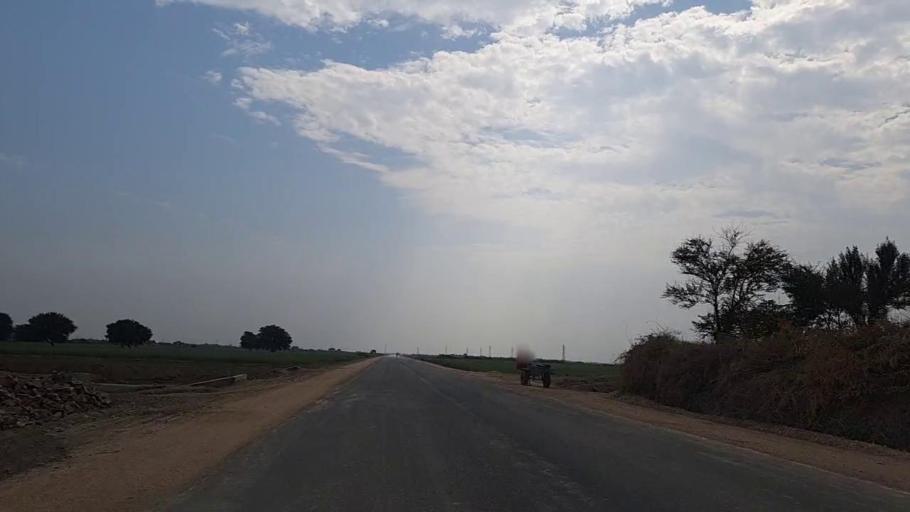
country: PK
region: Sindh
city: Naukot
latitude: 24.9680
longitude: 69.2827
